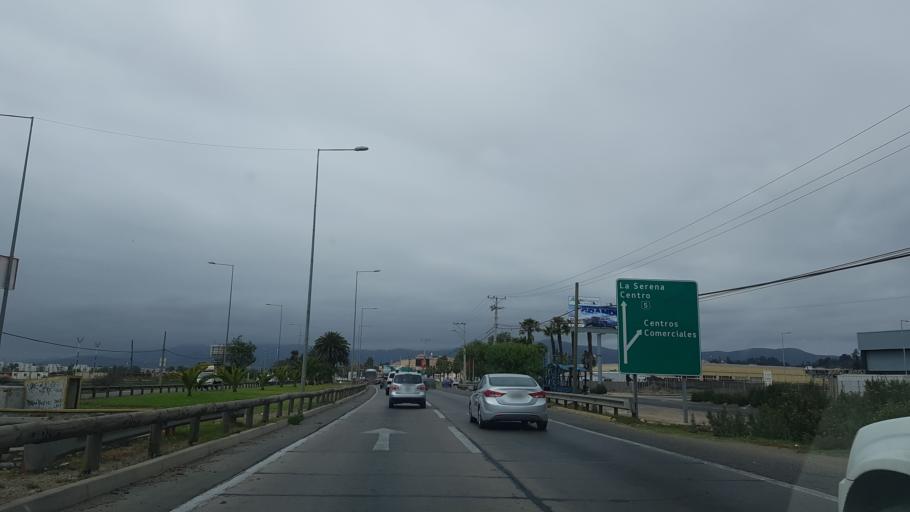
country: CL
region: Coquimbo
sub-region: Provincia de Elqui
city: La Serena
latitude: -29.9184
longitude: -71.2630
